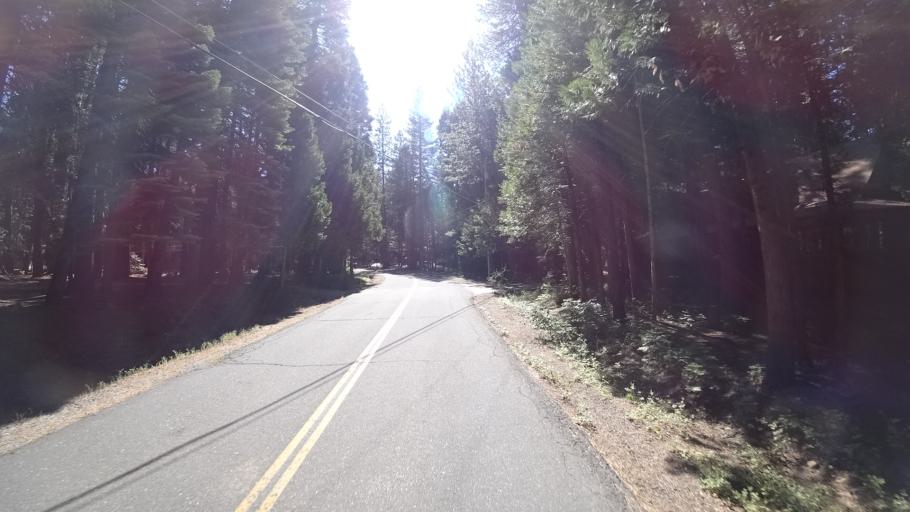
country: US
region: California
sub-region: Calaveras County
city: Arnold
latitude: 38.2911
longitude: -120.2704
